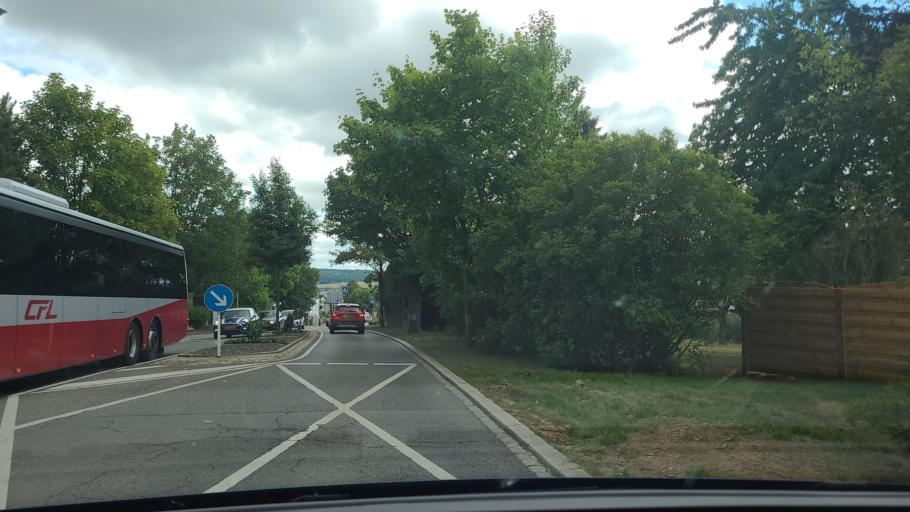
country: LU
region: Luxembourg
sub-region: Canton de Luxembourg
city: Hesperange
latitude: 49.5725
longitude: 6.1436
